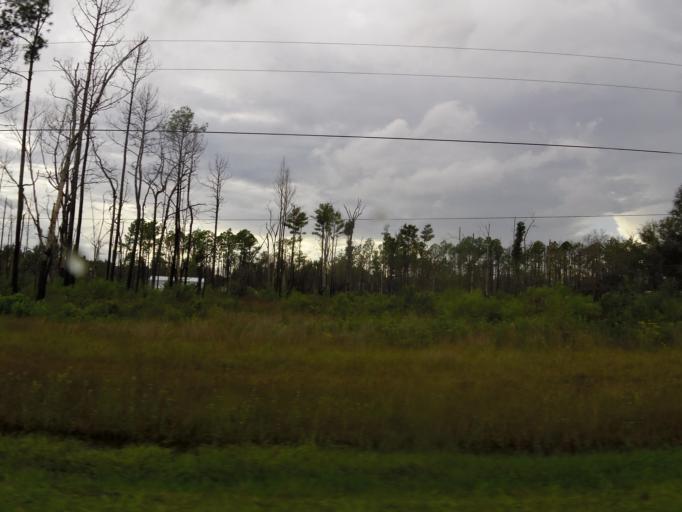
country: US
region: Florida
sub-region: Duval County
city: Baldwin
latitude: 30.4102
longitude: -82.0270
